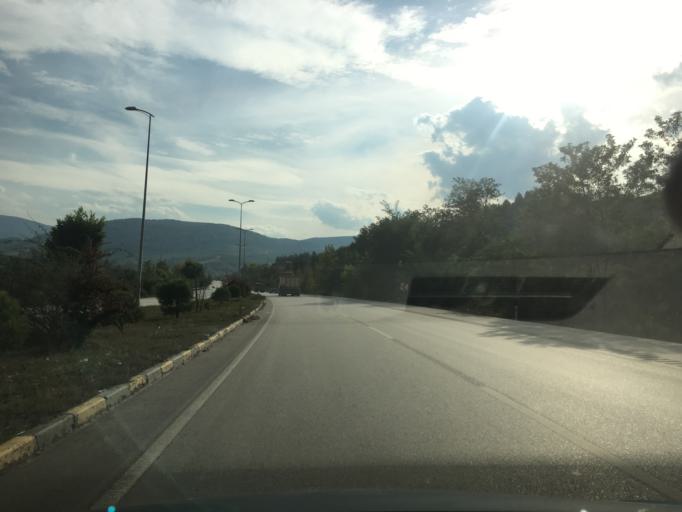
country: TR
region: Karabuk
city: Karabuk
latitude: 41.1182
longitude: 32.6735
